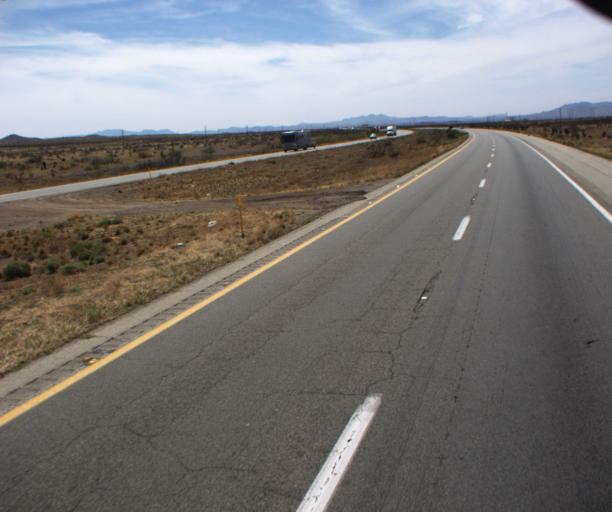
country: US
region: Arizona
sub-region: Cochise County
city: Willcox
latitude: 32.3479
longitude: -109.7450
